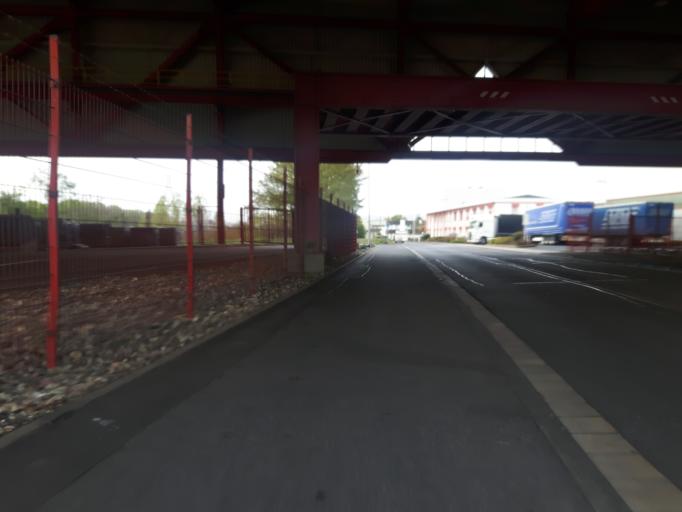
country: DE
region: Rheinland-Pfalz
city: Neuwied
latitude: 50.4180
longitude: 7.4701
